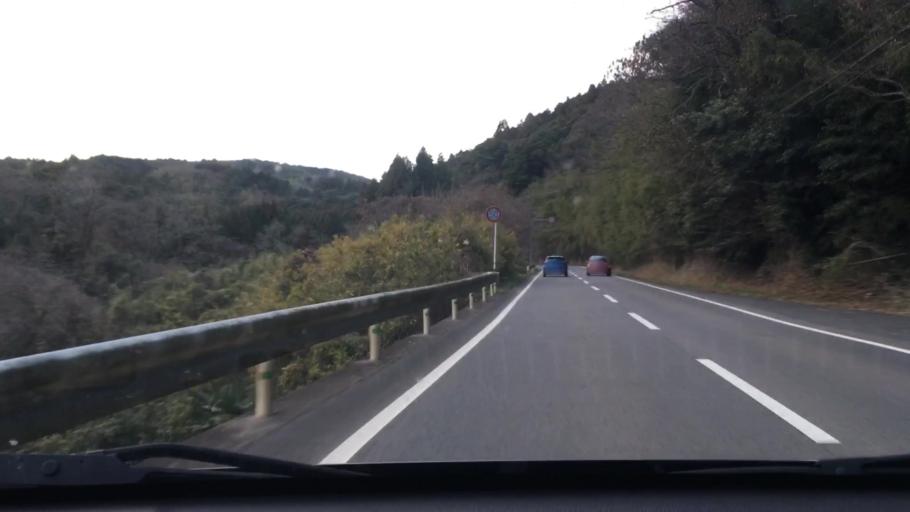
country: JP
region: Oita
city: Hiji
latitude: 33.3702
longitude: 131.4649
